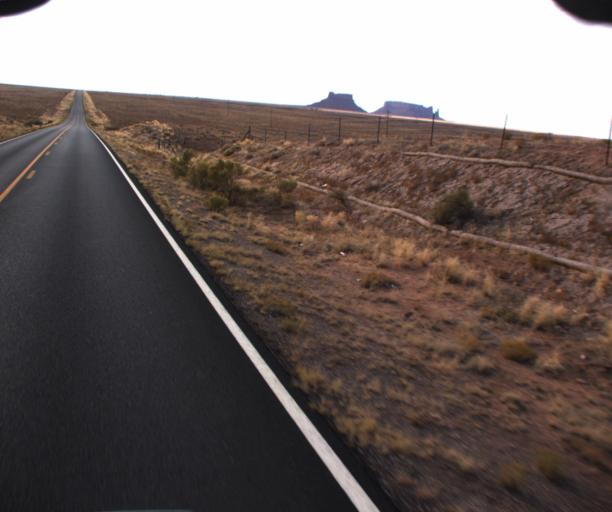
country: US
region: Arizona
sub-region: Apache County
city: Many Farms
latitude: 36.5822
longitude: -109.5560
